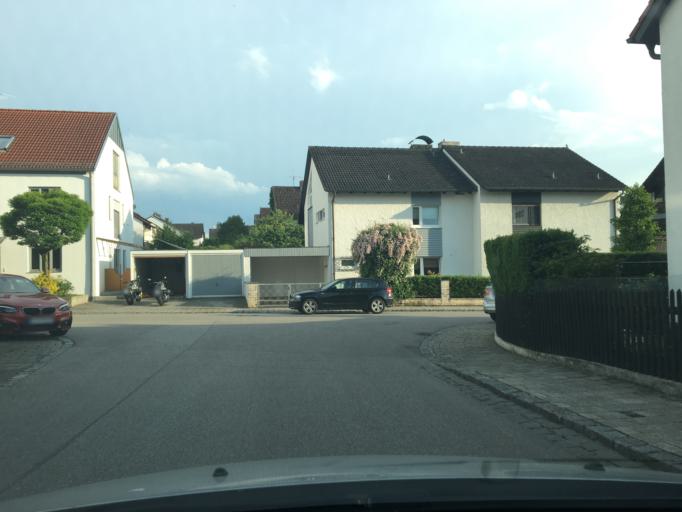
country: DE
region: Bavaria
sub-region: Upper Bavaria
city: Haimhausen
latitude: 48.3147
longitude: 11.5588
